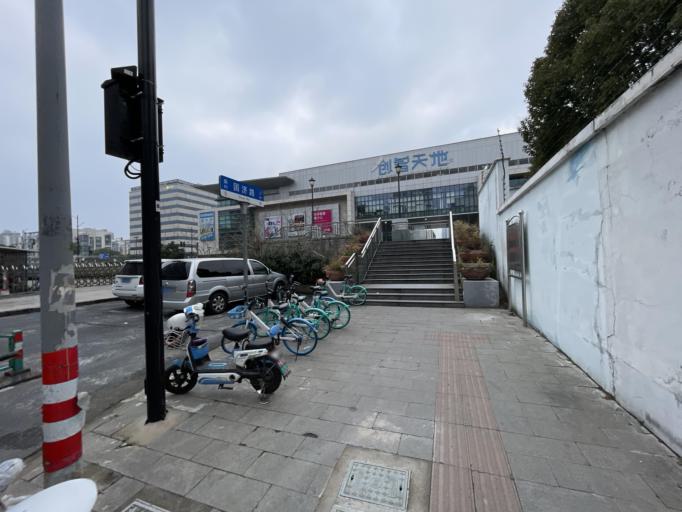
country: CN
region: Shanghai Shi
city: Yangpu
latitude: 31.3063
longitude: 121.5101
